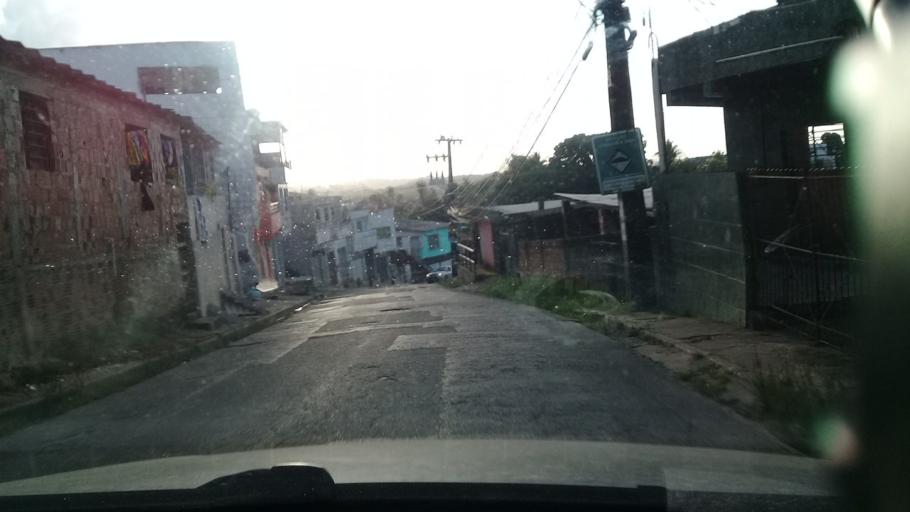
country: BR
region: Pernambuco
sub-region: Jaboatao Dos Guararapes
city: Jaboatao dos Guararapes
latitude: -8.1089
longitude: -34.9620
